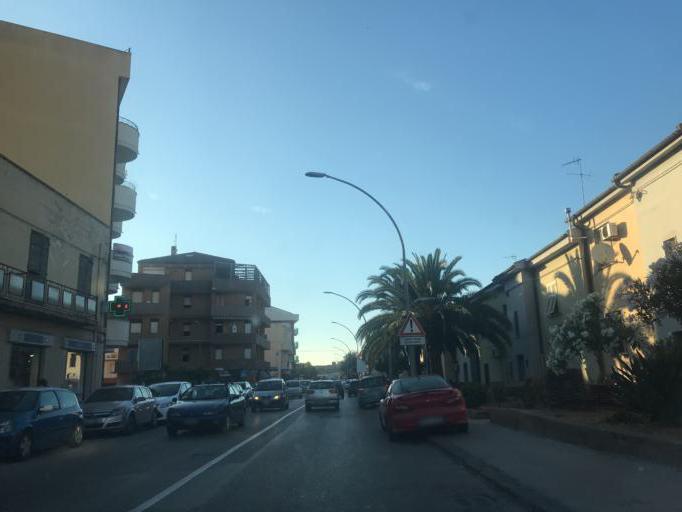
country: IT
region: Sardinia
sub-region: Provincia di Sassari
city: Alghero
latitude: 40.5751
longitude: 8.3213
